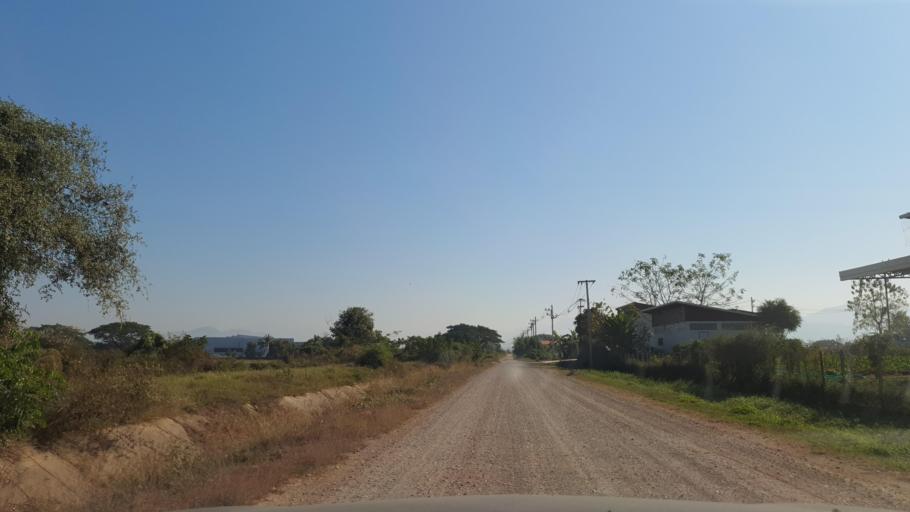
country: TH
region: Chiang Mai
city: San Kamphaeng
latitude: 18.7048
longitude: 99.1384
